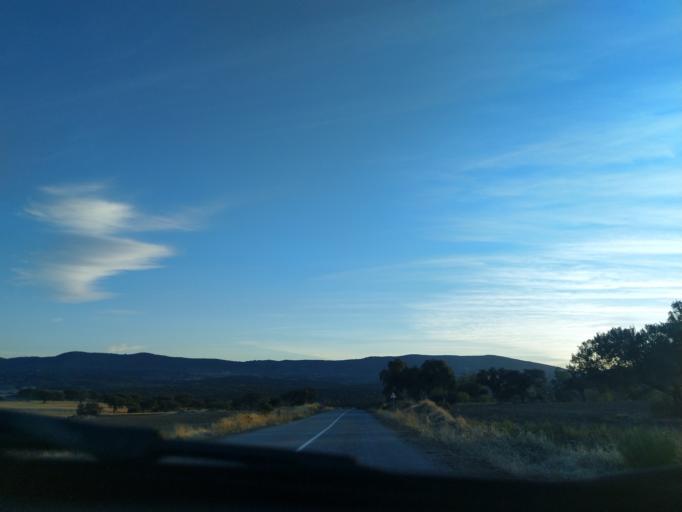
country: ES
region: Extremadura
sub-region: Provincia de Badajoz
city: Valverde de Llerena
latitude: 38.1847
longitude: -5.8608
